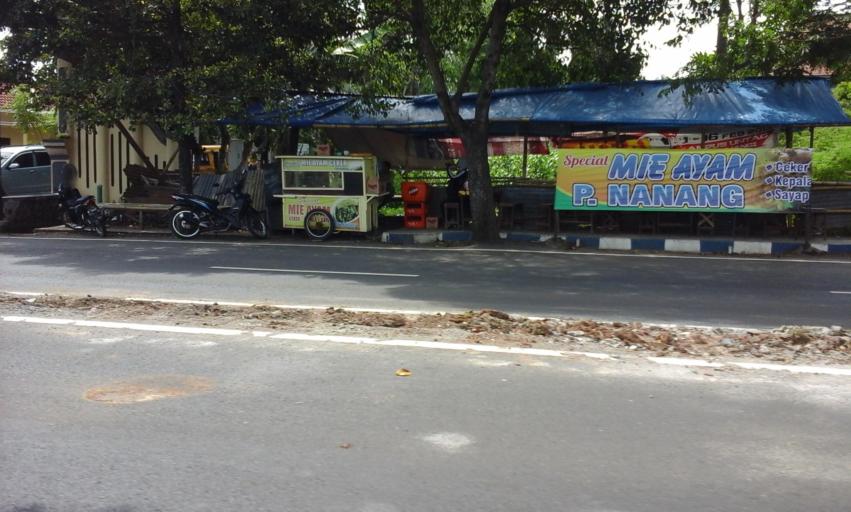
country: ID
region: East Java
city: Cungking
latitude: -8.2218
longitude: 114.3525
